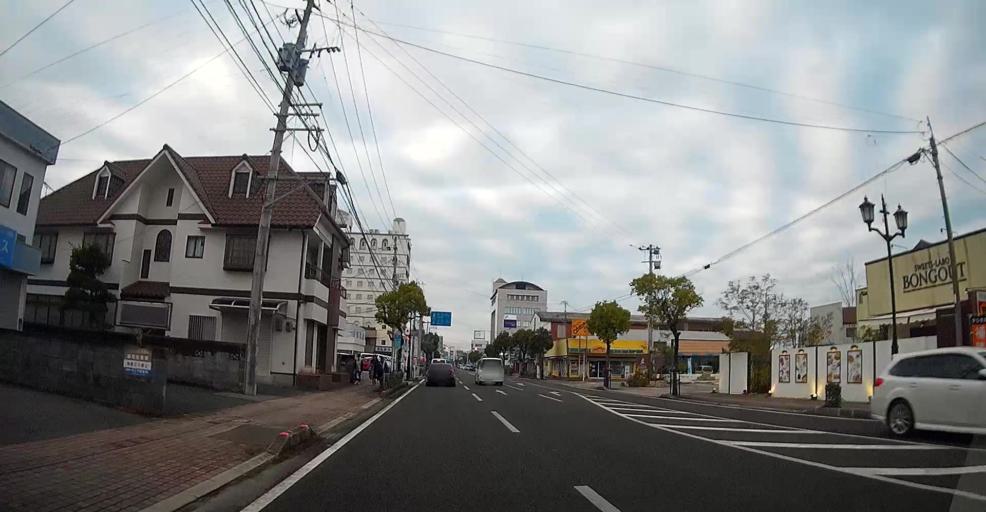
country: JP
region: Kumamoto
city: Hondo
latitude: 32.4501
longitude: 130.1986
